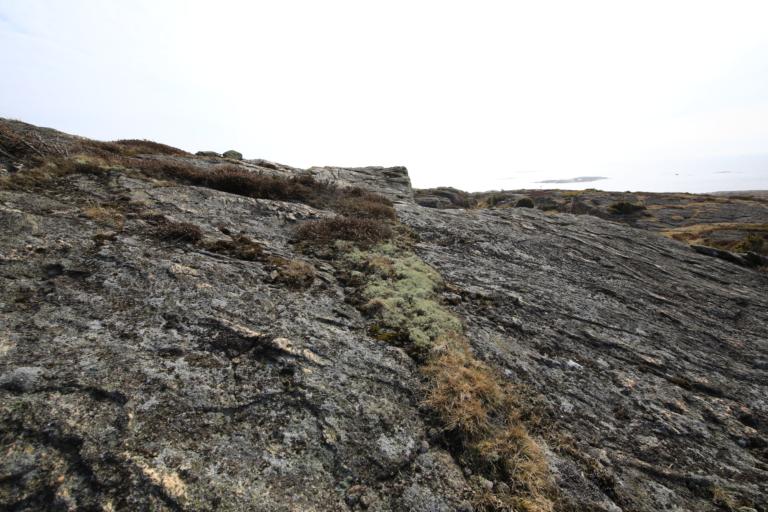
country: SE
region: Halland
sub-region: Kungsbacka Kommun
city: Frillesas
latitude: 57.2544
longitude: 12.0923
